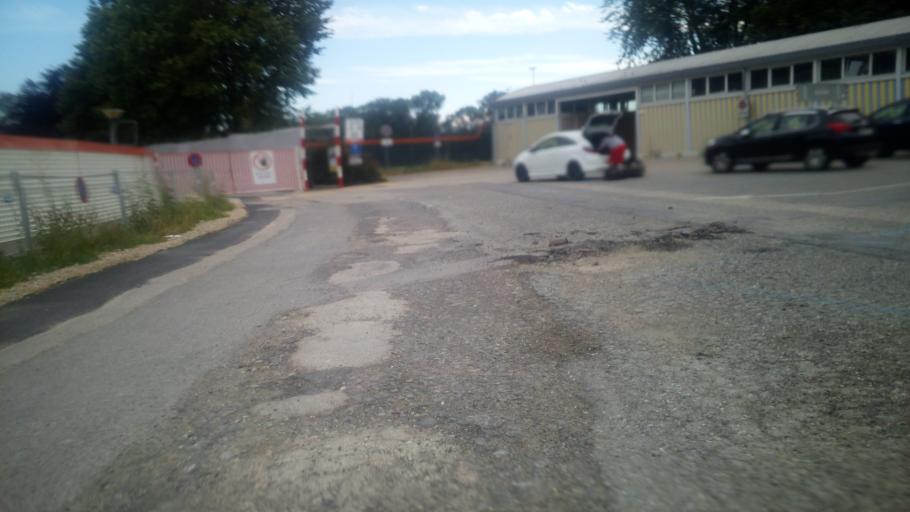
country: CH
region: Vaud
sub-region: Ouest Lausannois District
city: Chavannes
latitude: 46.5251
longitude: 6.5741
